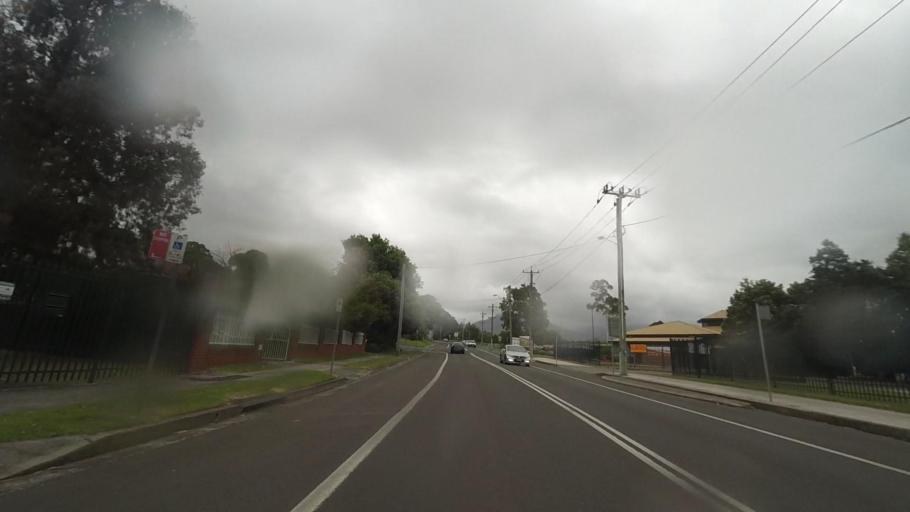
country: AU
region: New South Wales
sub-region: Wollongong
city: Cordeaux Heights
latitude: -34.4400
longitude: 150.8538
